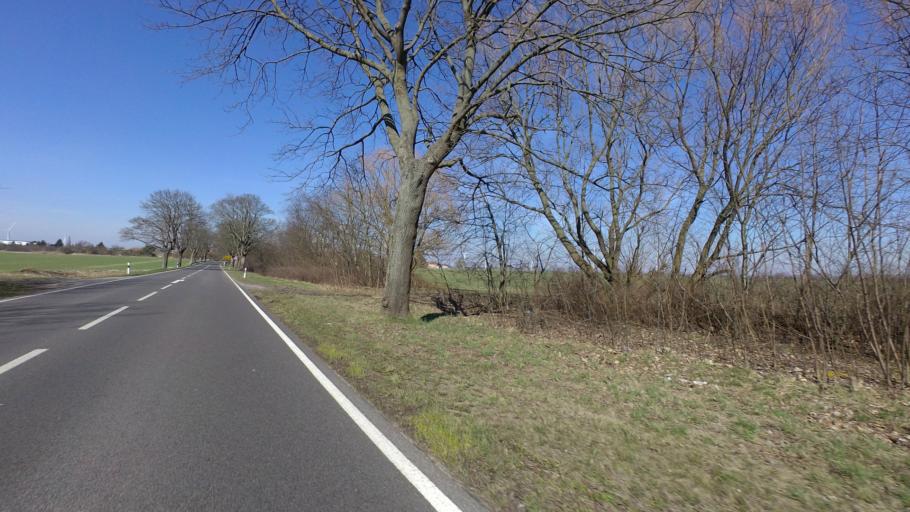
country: DE
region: Brandenburg
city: Werftpfuhl
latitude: 52.7322
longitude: 13.8379
